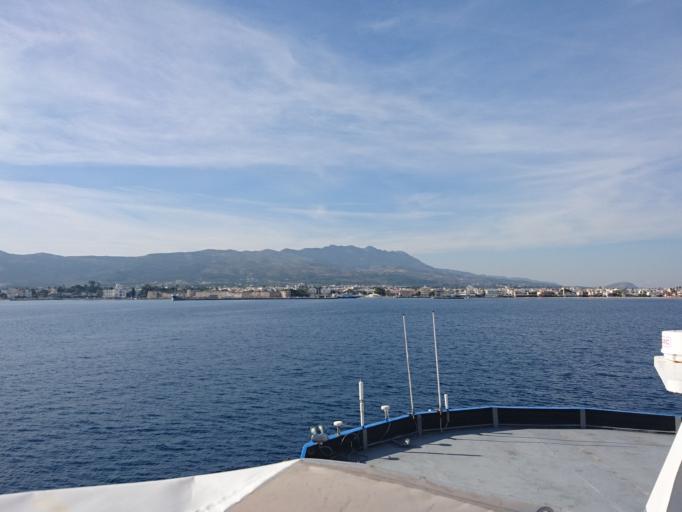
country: GR
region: South Aegean
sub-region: Nomos Dodekanisou
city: Kos
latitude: 36.9039
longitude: 27.2954
